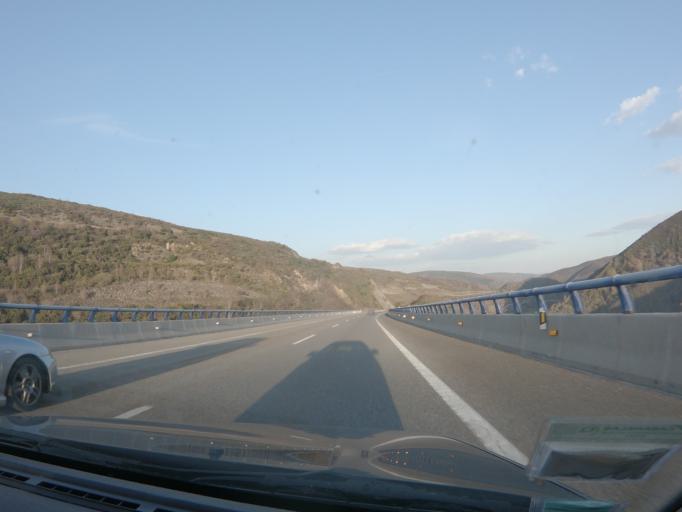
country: ES
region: Castille and Leon
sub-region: Provincia de Leon
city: Vega de Valcarce
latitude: 42.6744
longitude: -6.9801
